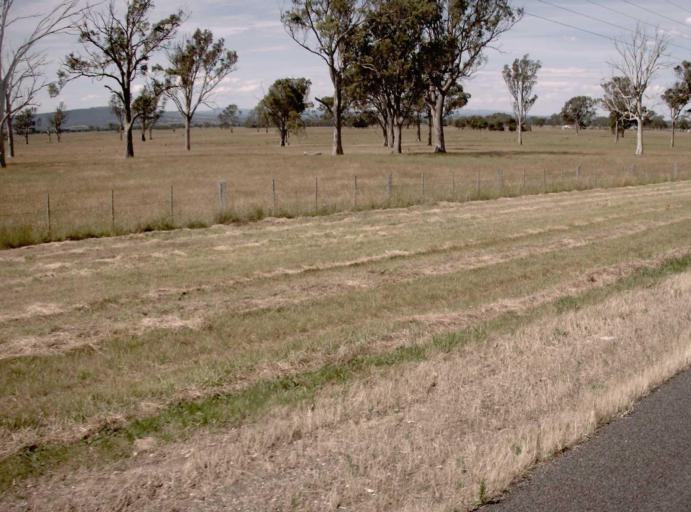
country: AU
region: Victoria
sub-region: East Gippsland
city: Bairnsdale
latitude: -37.8641
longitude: 147.4992
